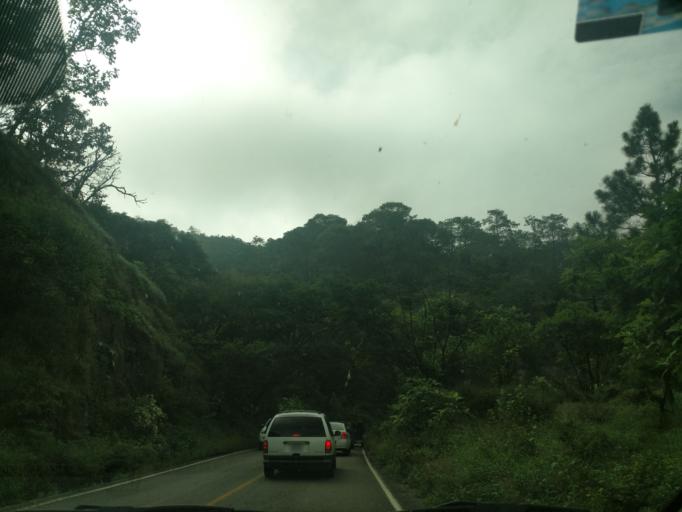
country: MX
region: Jalisco
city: El Salto
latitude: 20.4594
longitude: -104.3911
